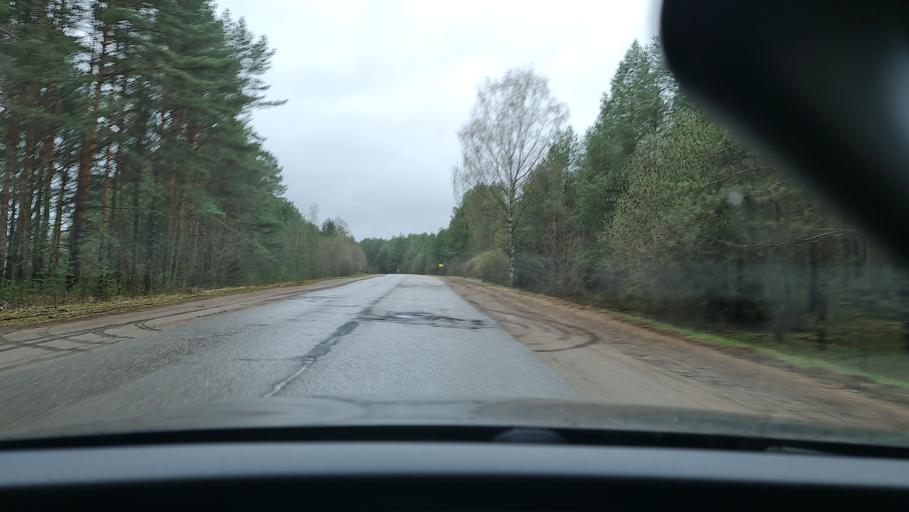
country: RU
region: Novgorod
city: Demyansk
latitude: 57.6574
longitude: 32.4914
